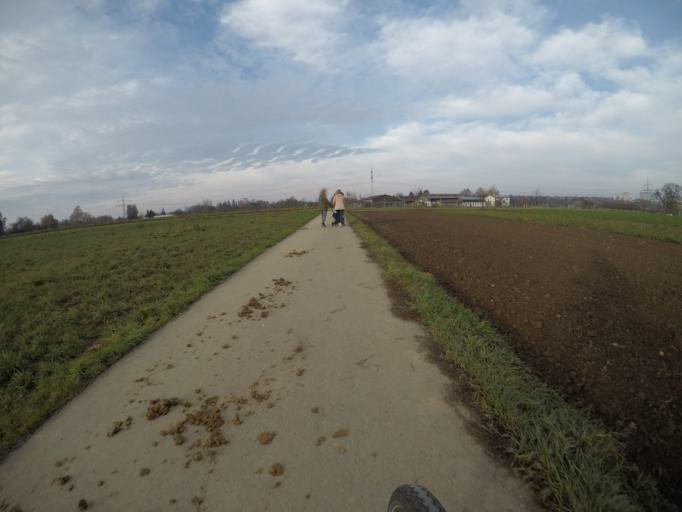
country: DE
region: Baden-Wuerttemberg
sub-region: Regierungsbezirk Stuttgart
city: Leinfelden-Echterdingen
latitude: 48.7134
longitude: 9.1455
